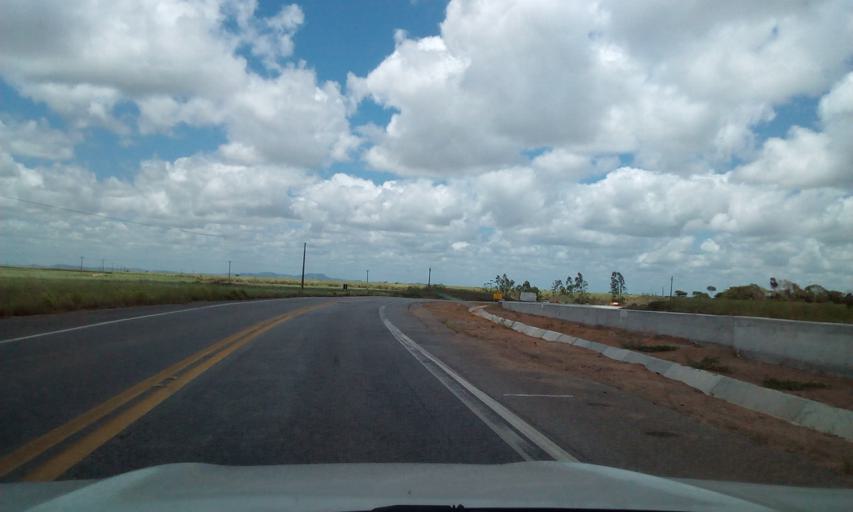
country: BR
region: Alagoas
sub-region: Sao Miguel Dos Campos
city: Sao Miguel dos Campos
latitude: -9.8581
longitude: -36.1448
